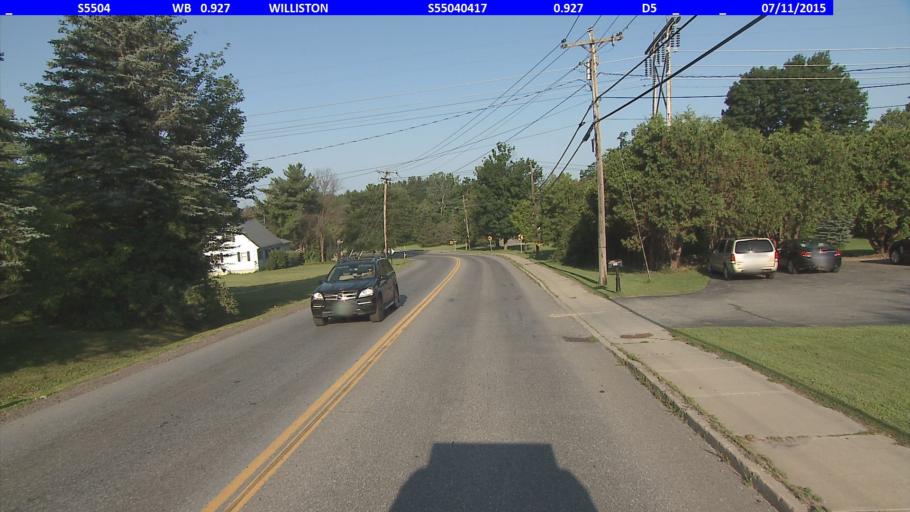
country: US
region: Vermont
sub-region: Chittenden County
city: Essex Junction
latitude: 44.4649
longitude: -73.1153
